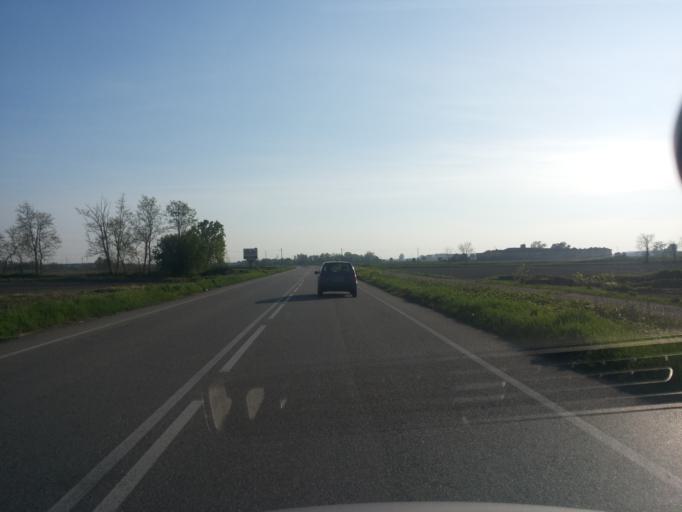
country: IT
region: Lombardy
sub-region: Provincia di Pavia
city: Mortara
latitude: 45.2597
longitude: 8.7173
